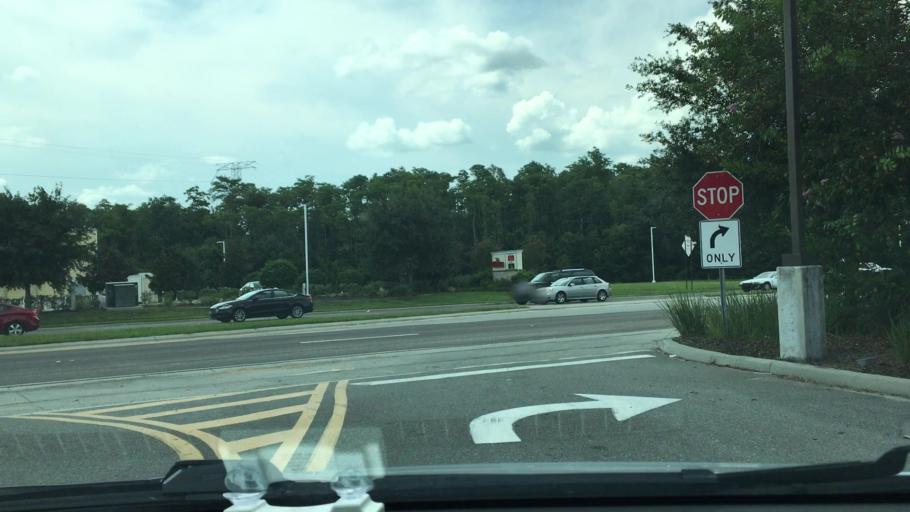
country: US
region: Florida
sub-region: Orange County
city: Conway
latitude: 28.4797
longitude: -81.2872
